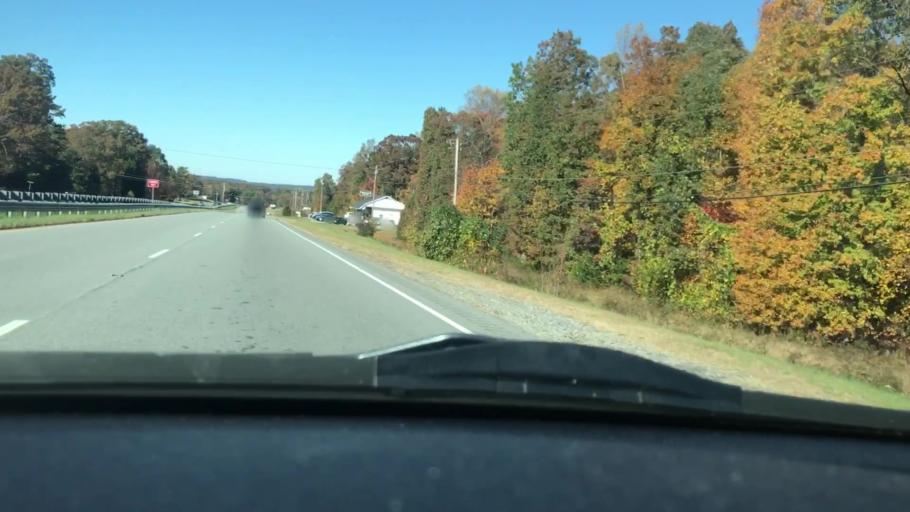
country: US
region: North Carolina
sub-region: Rockingham County
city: Madison
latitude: 36.3474
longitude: -79.9448
